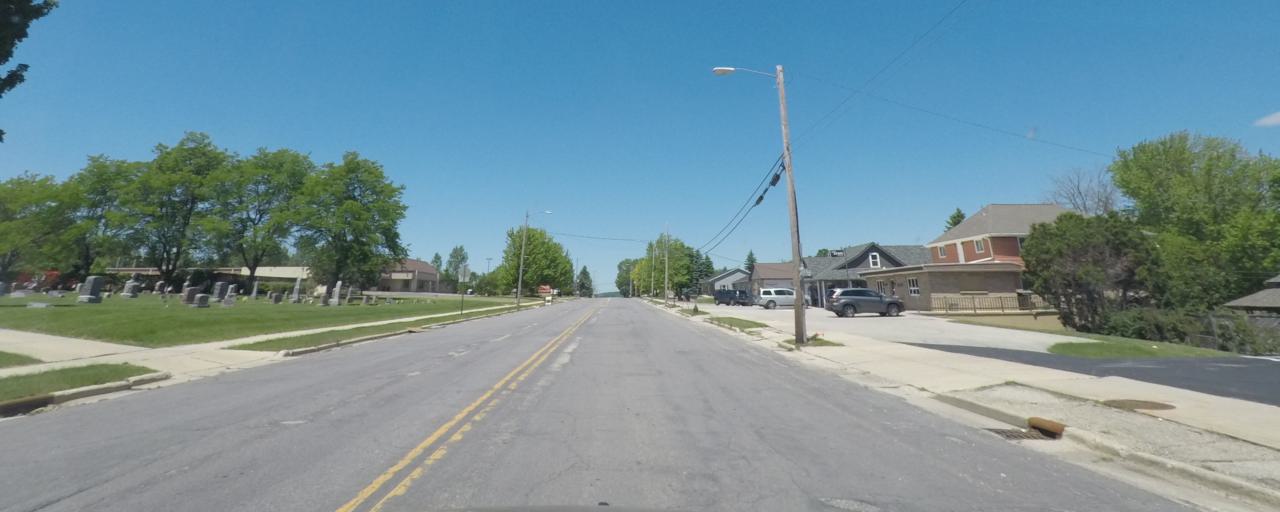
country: US
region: Wisconsin
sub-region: Washington County
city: West Bend
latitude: 43.4435
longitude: -88.1881
